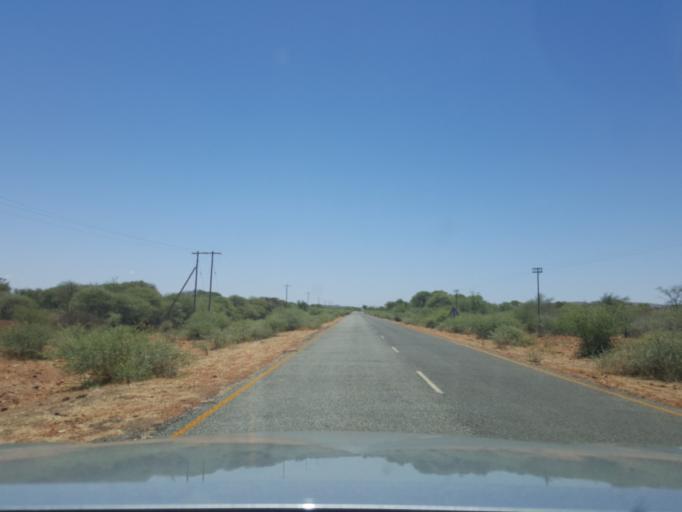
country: BW
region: South East
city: Ramotswa
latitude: -24.8824
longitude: 25.8908
